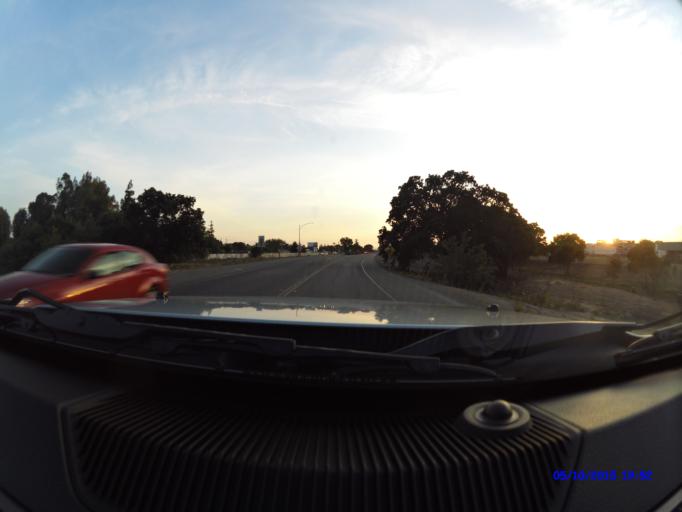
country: US
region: California
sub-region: San Joaquin County
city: Kennedy
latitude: 37.9462
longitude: -121.2517
